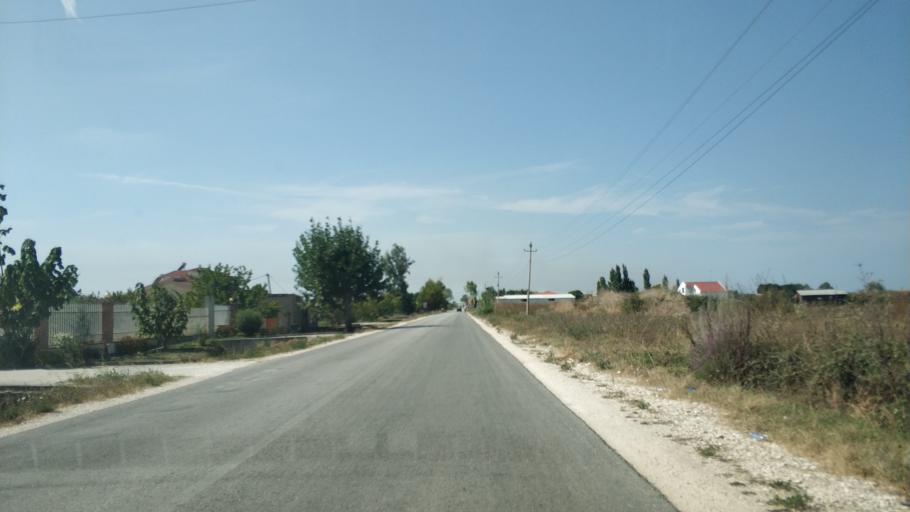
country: AL
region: Fier
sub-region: Rrethi i Fierit
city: Dermenas
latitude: 40.7395
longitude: 19.5118
